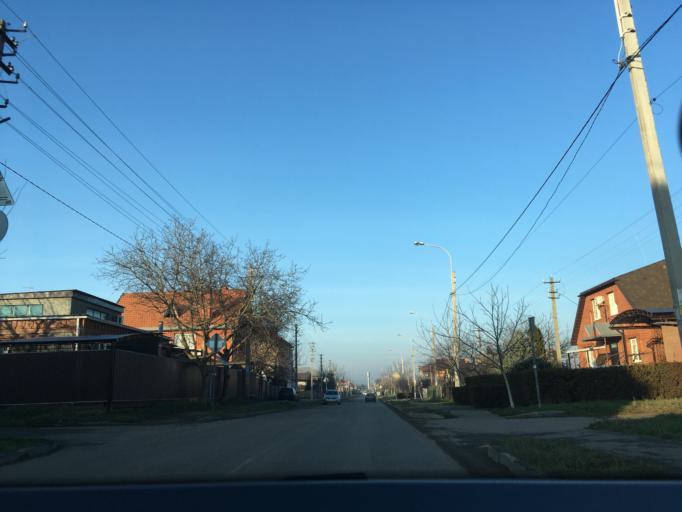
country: RU
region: Krasnodarskiy
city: Krasnodar
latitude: 45.1201
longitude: 39.0143
